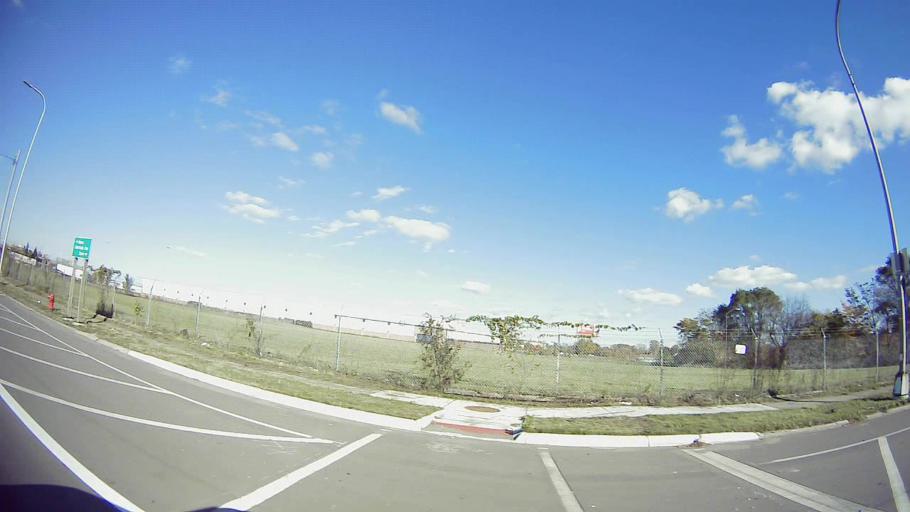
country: US
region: Michigan
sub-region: Wayne County
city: Dearborn
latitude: 42.3381
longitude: -83.1253
